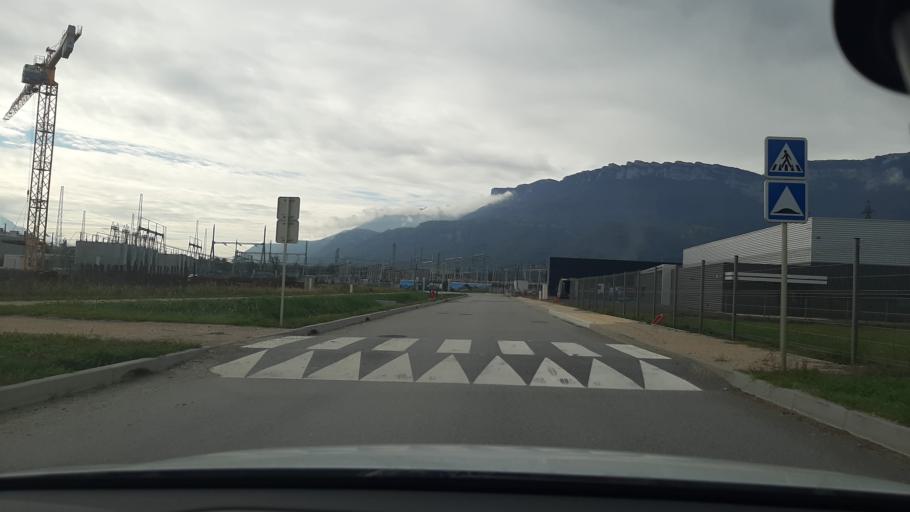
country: FR
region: Rhone-Alpes
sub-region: Departement de la Savoie
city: Montmelian
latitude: 45.4737
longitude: 6.0322
